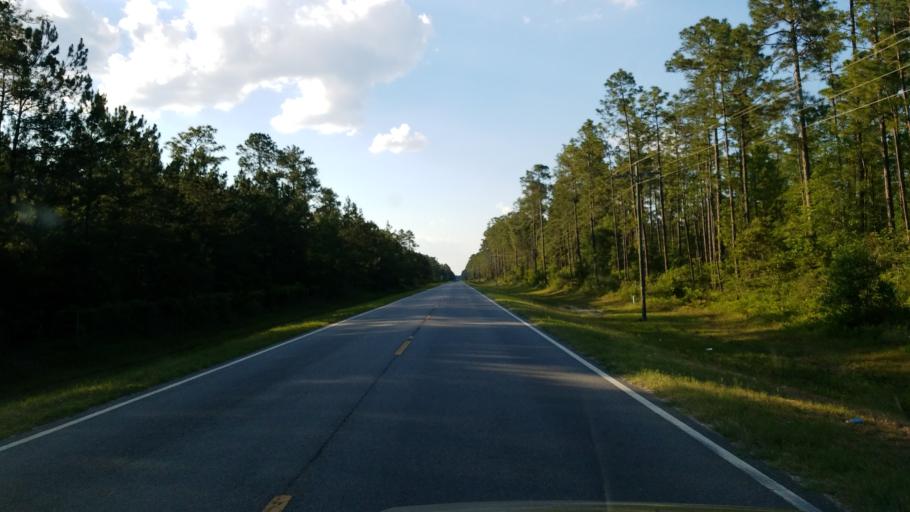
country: US
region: Georgia
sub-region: Lanier County
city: Lakeland
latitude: 31.0993
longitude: -83.0791
